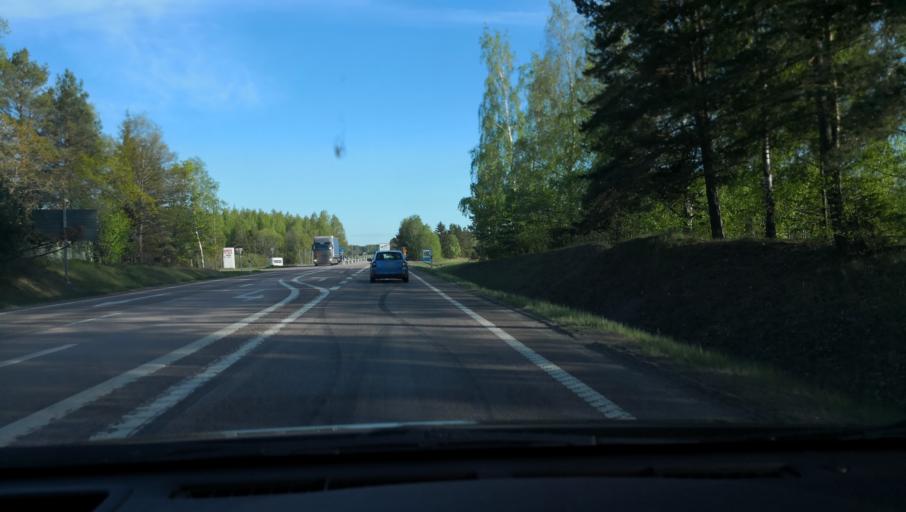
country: SE
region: Vaestmanland
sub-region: Vasteras
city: Hokasen
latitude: 59.6916
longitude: 16.5768
